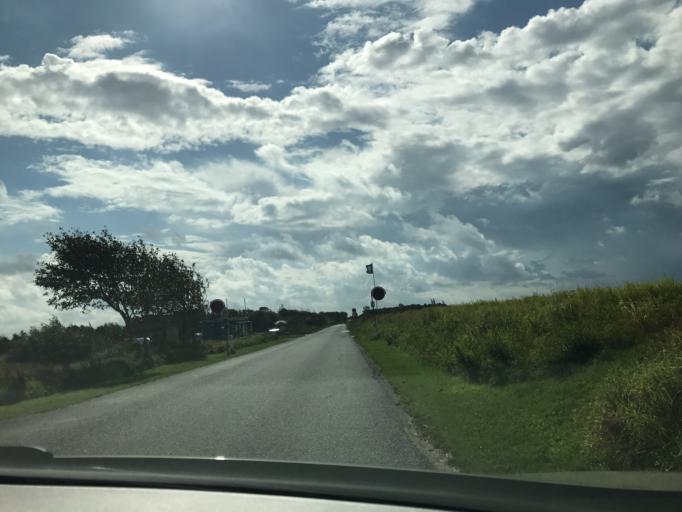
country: DK
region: South Denmark
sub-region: Middelfart Kommune
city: Norre Aby
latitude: 55.4220
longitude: 9.8291
